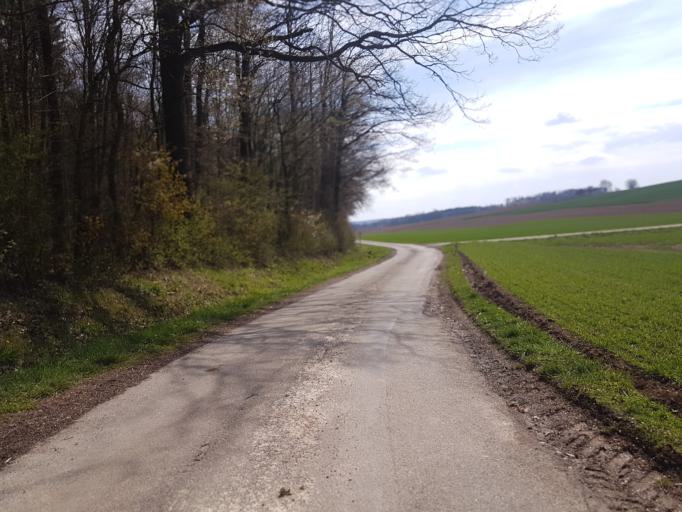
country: DE
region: Baden-Wuerttemberg
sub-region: Regierungsbezirk Stuttgart
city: Jagsthausen
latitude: 49.3771
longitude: 9.5192
